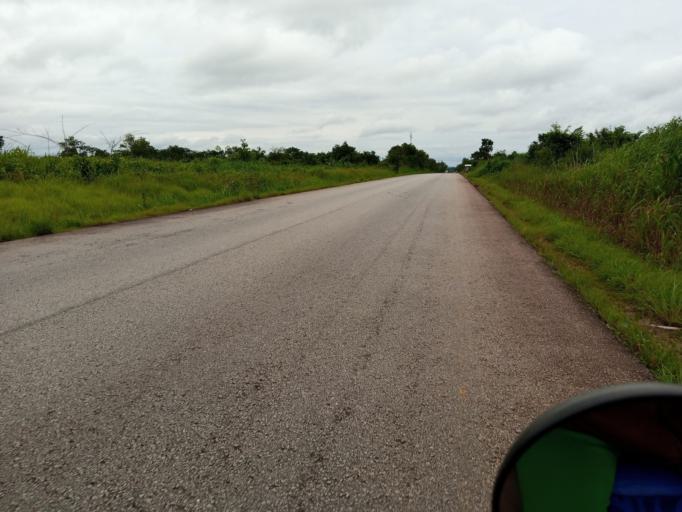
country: SL
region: Southern Province
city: Largo
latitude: 8.1959
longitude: -12.0470
